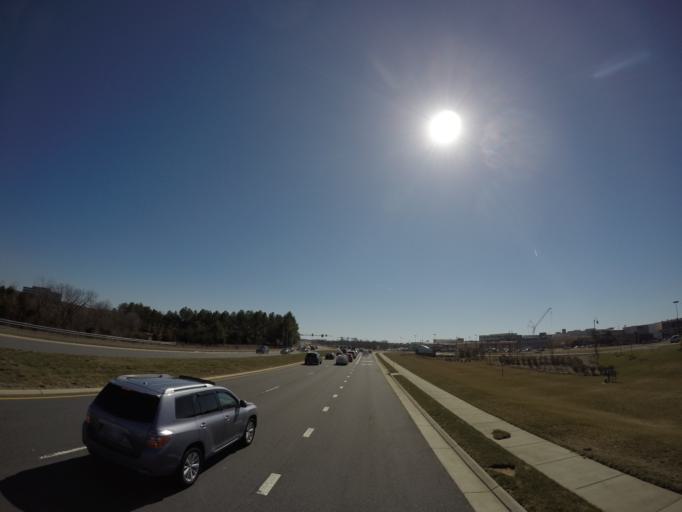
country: US
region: Virginia
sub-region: Loudoun County
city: University Center
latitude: 39.0536
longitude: -77.4515
